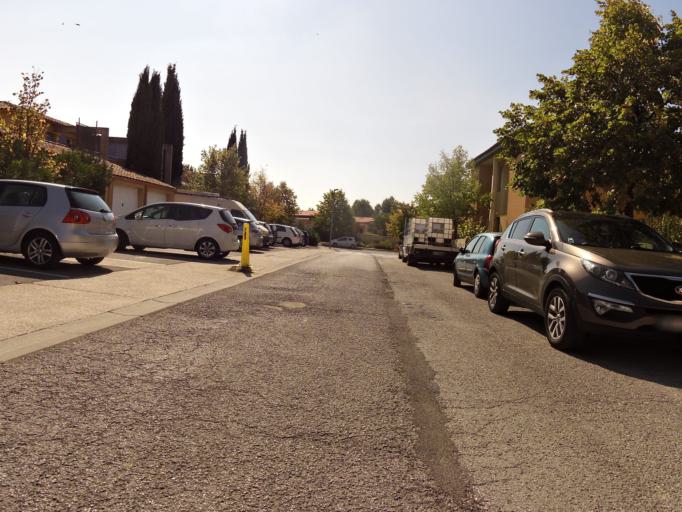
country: FR
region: Languedoc-Roussillon
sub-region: Departement du Gard
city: Calvisson
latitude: 43.7872
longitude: 4.1971
